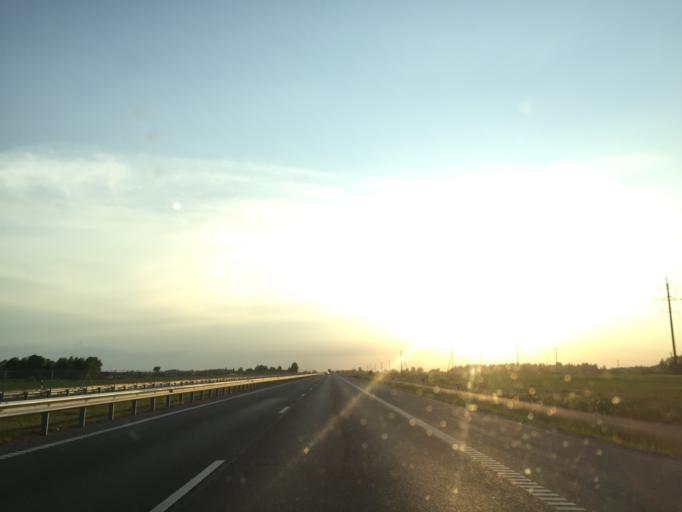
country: LT
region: Siauliu apskritis
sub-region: Siauliai
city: Siauliai
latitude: 55.9611
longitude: 23.2324
